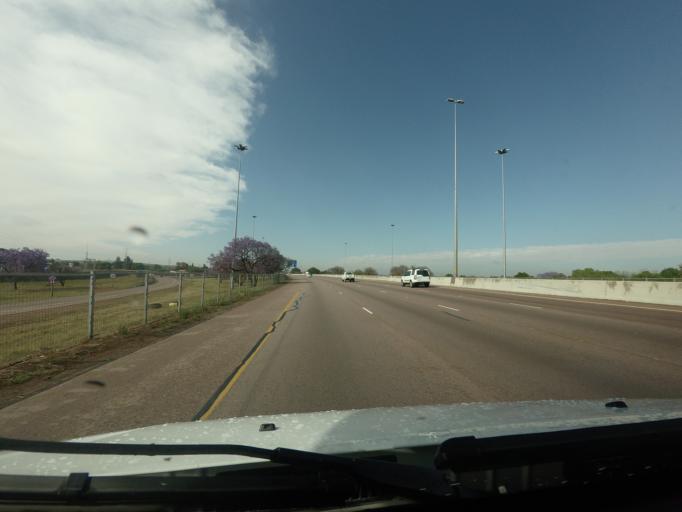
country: ZA
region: Gauteng
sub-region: City of Tshwane Metropolitan Municipality
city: Pretoria
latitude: -25.7091
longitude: 28.2664
